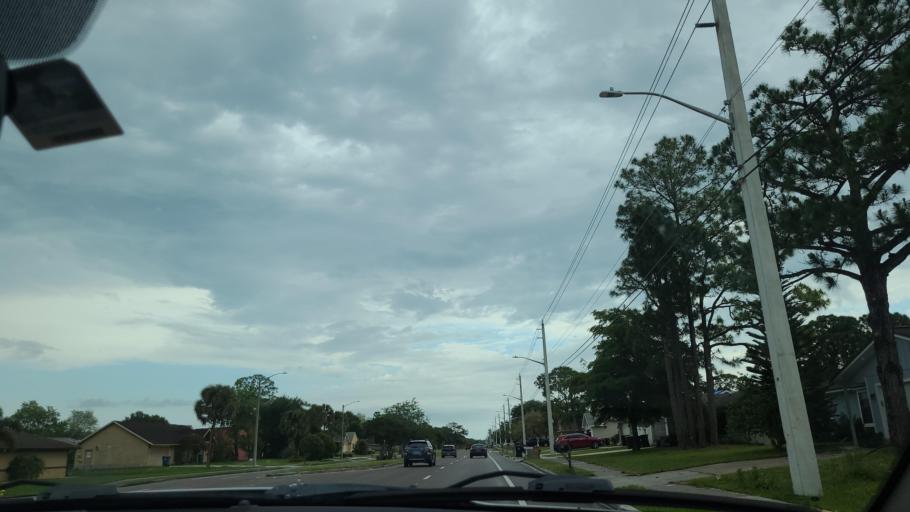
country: US
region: Florida
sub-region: Brevard County
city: June Park
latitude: 28.0319
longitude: -80.6874
